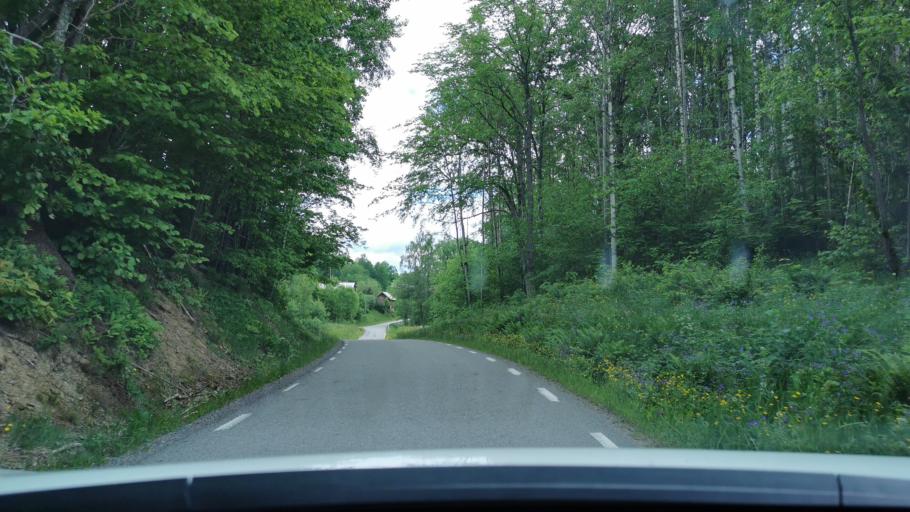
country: SE
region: Vaestra Goetaland
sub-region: Bengtsfors Kommun
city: Dals Langed
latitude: 58.8382
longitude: 12.3302
